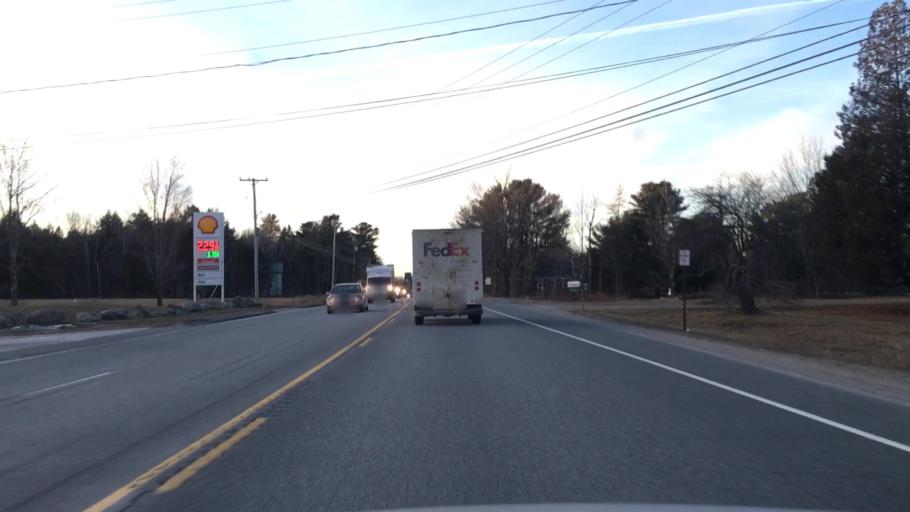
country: US
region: Maine
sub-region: Penobscot County
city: Holden
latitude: 44.7499
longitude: -68.6496
